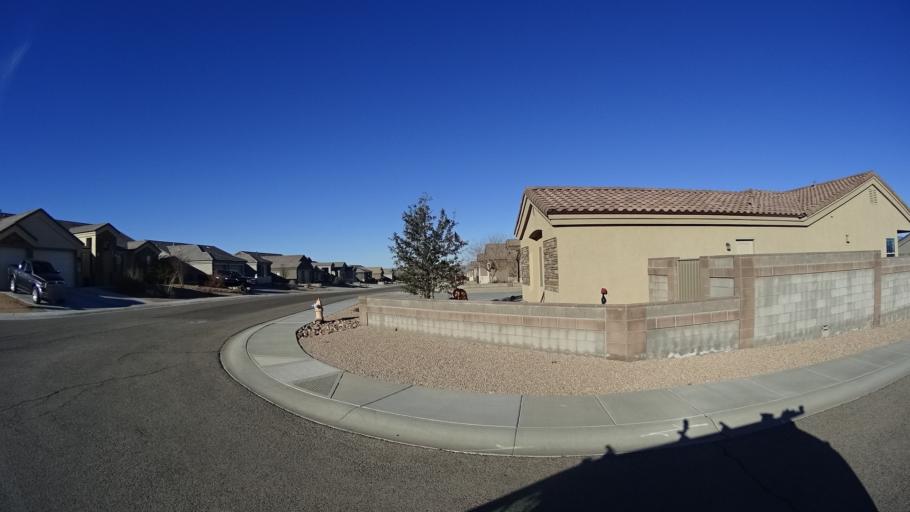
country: US
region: Arizona
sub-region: Mohave County
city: Kingman
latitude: 35.1923
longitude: -113.9944
